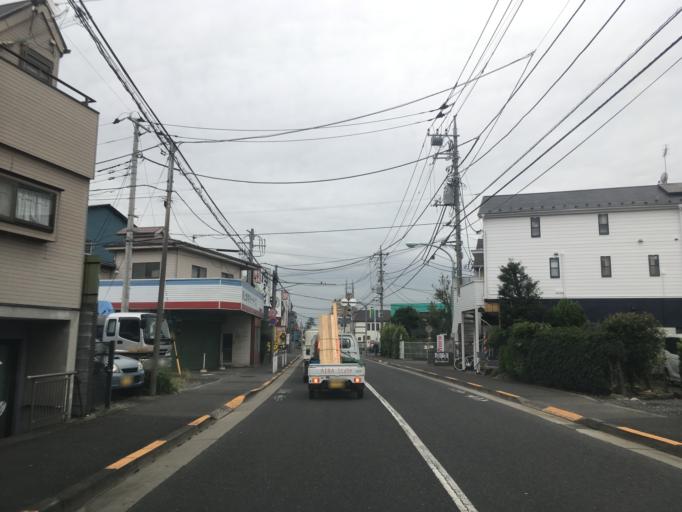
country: JP
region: Tokyo
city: Kokubunji
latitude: 35.7197
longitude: 139.4648
